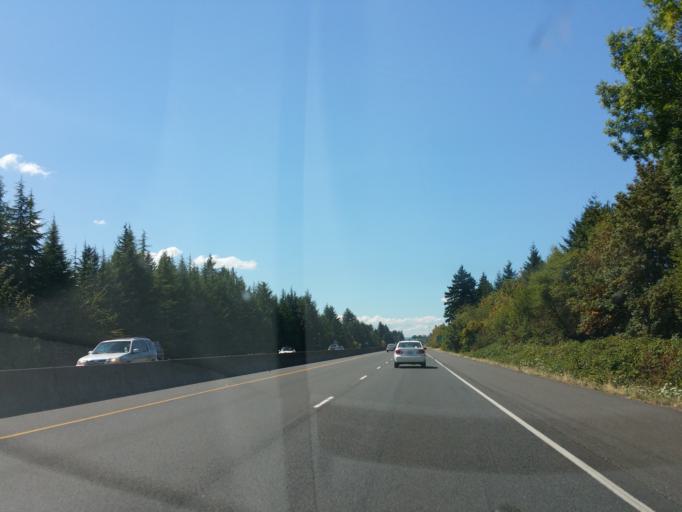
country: US
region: Washington
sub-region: Clark County
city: Mill Plain
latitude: 45.5985
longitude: -122.5290
